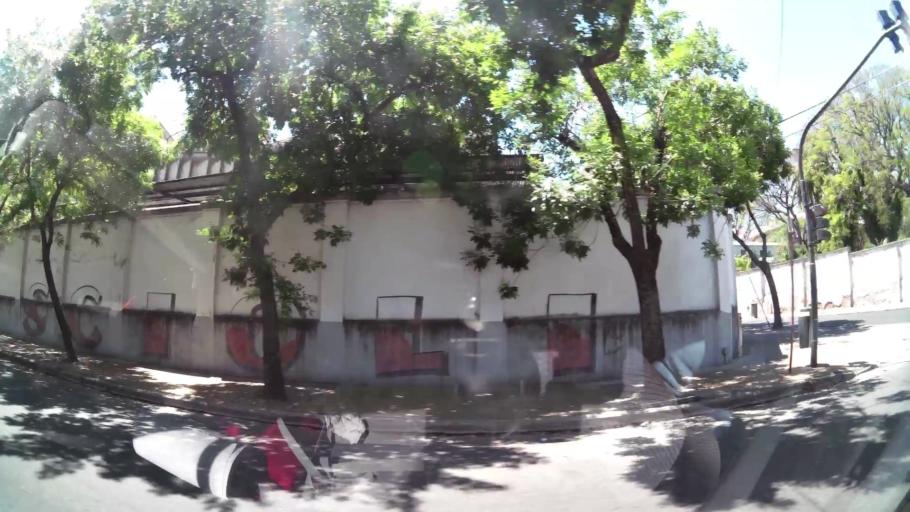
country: AR
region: Buenos Aires F.D.
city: Buenos Aires
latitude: -34.6394
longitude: -58.3866
